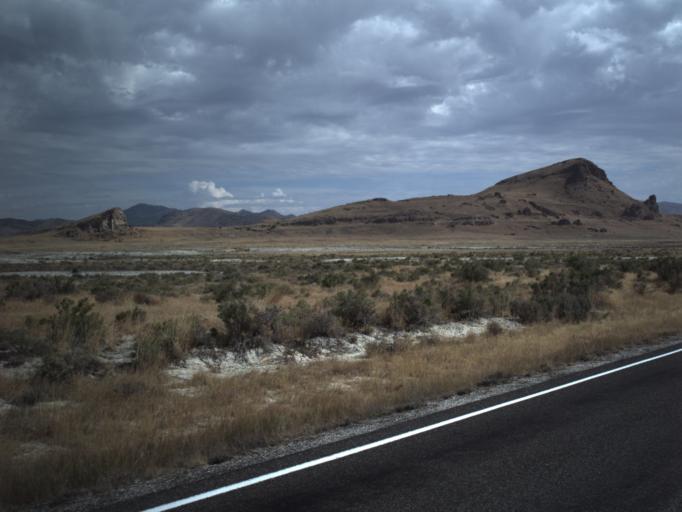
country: US
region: Utah
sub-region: Tooele County
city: Wendover
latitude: 41.4247
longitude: -113.8590
